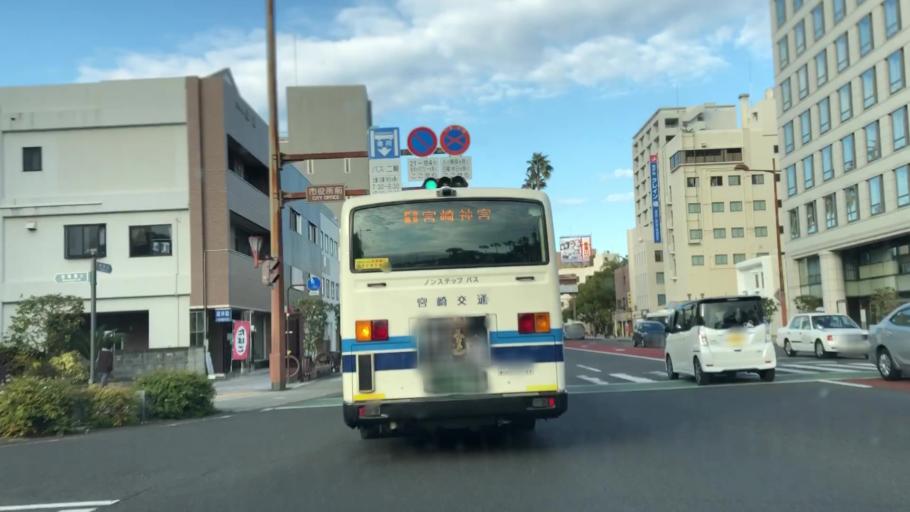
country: JP
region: Miyazaki
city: Miyazaki-shi
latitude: 31.9085
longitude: 131.4215
